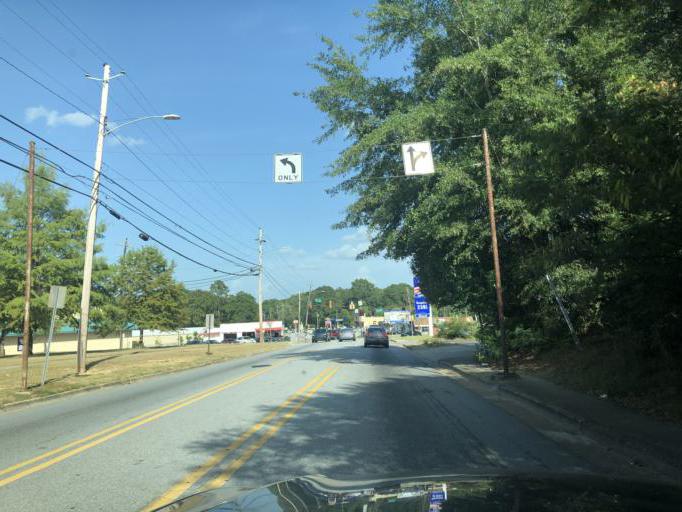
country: US
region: Georgia
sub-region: Muscogee County
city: Columbus
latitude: 32.4841
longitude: -84.9260
